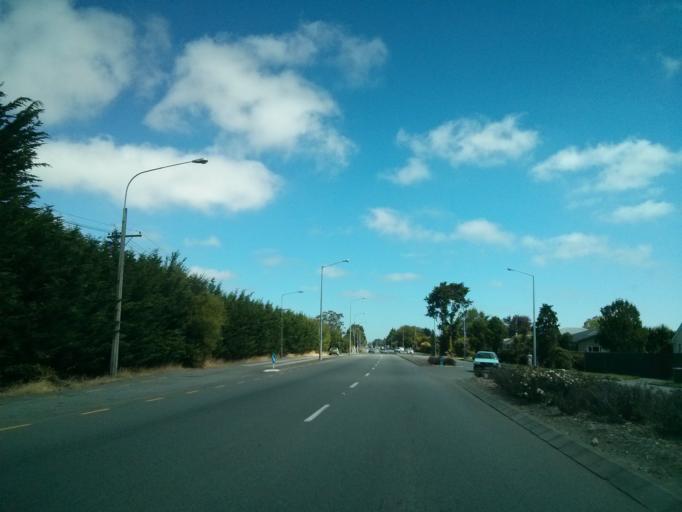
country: NZ
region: Canterbury
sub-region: Waimakariri District
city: Kaiapoi
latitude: -43.4388
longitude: 172.6366
